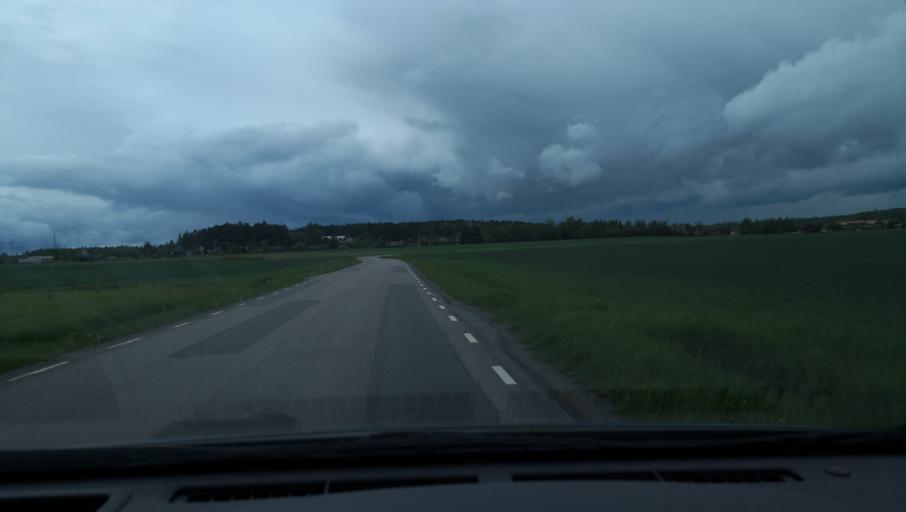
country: SE
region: Uppsala
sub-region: Enkopings Kommun
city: Orsundsbro
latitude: 59.7250
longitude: 17.3126
